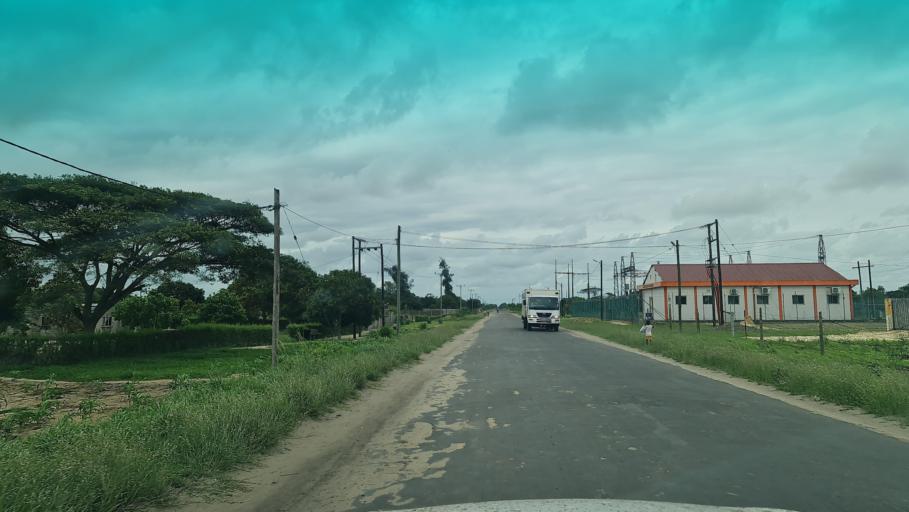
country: MZ
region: Maputo
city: Manhica
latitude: -25.4341
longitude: 32.7732
